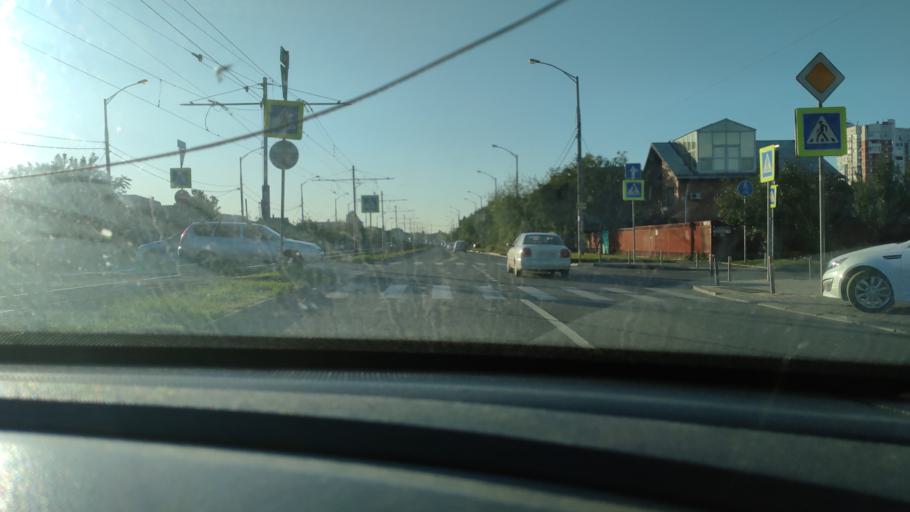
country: RU
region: Krasnodarskiy
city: Krasnodar
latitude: 45.0415
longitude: 38.9476
